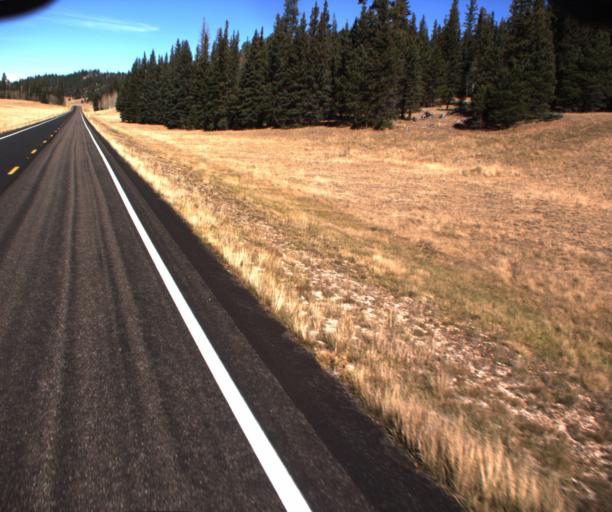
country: US
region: Arizona
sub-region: Coconino County
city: Grand Canyon
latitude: 36.4642
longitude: -112.1273
